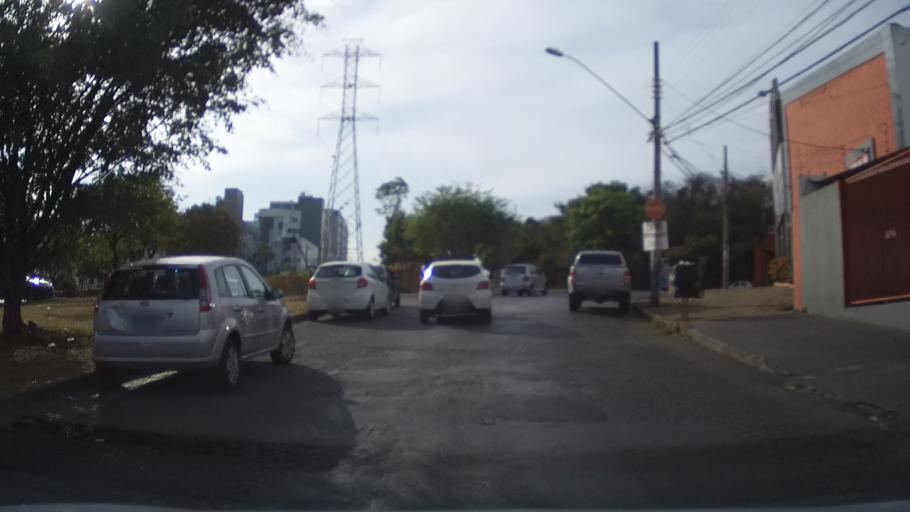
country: BR
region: Minas Gerais
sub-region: Contagem
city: Contagem
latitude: -19.8820
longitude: -44.0002
